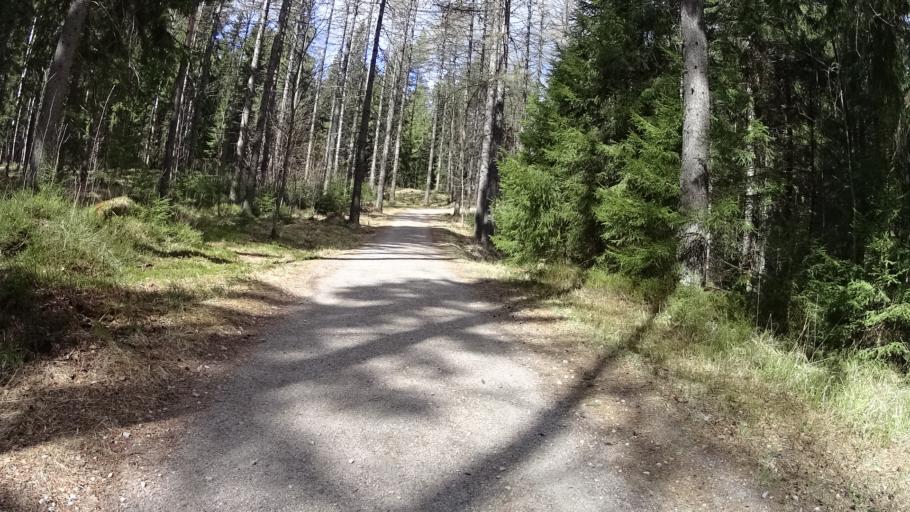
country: FI
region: Uusimaa
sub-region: Helsinki
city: Espoo
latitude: 60.2713
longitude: 24.6326
